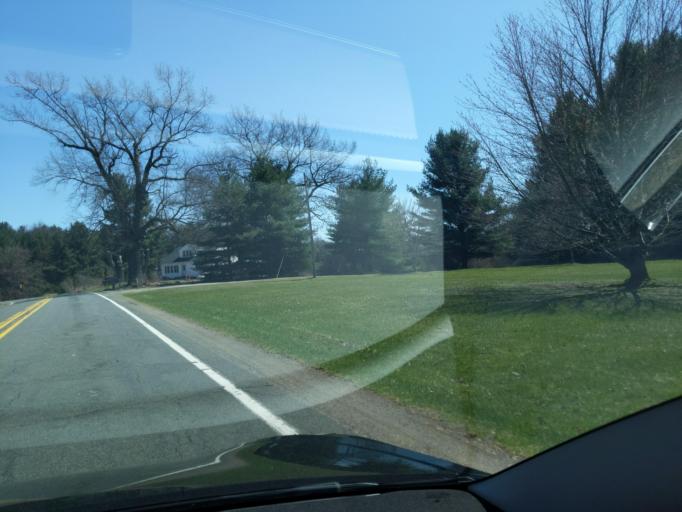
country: US
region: Michigan
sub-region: Ingham County
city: Mason
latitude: 42.5348
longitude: -84.3439
